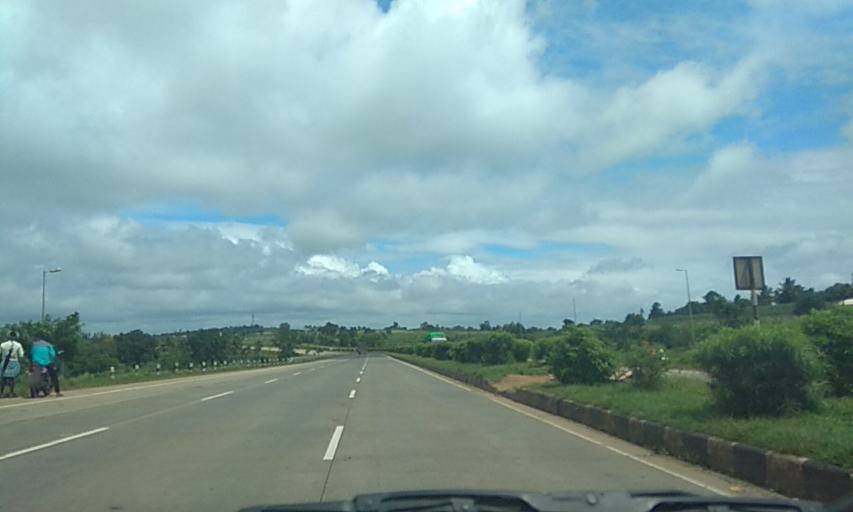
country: IN
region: Karnataka
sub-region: Dharwad
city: Alnavar
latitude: 15.6224
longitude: 74.7590
